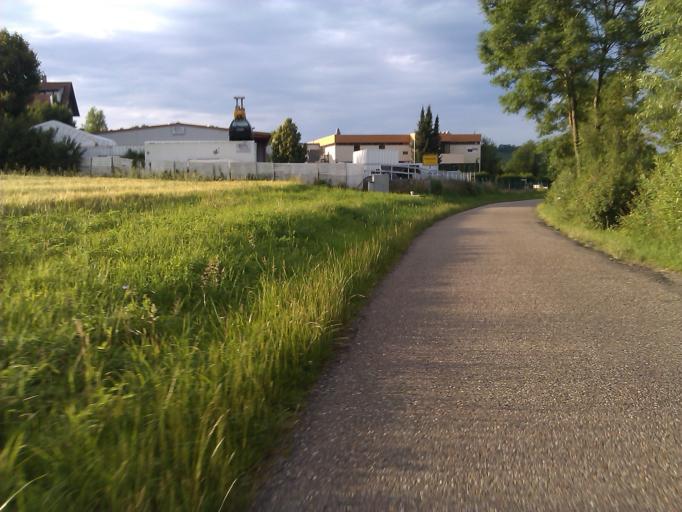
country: DE
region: Baden-Wuerttemberg
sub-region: Regierungsbezirk Stuttgart
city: Pfaffenhofen
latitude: 49.0573
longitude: 8.9756
